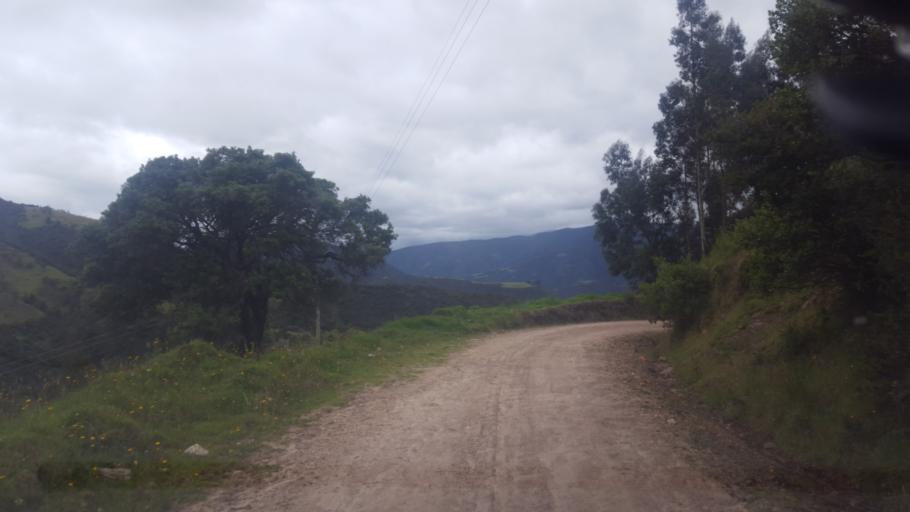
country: CO
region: Boyaca
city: Belen
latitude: 6.0311
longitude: -72.8825
